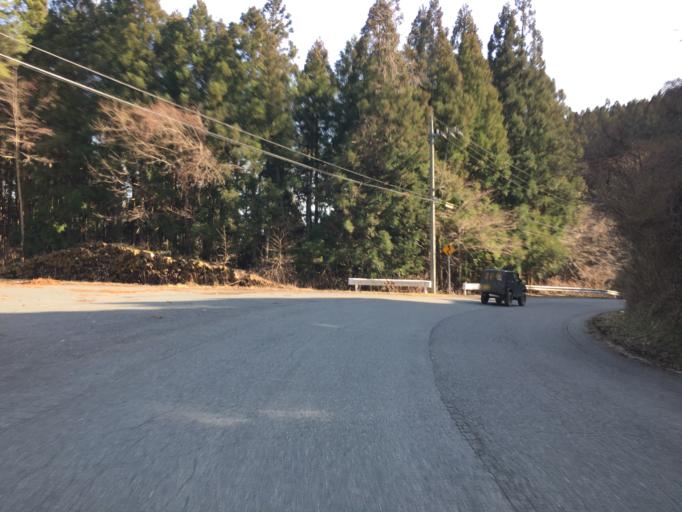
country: JP
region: Ibaraki
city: Takahagi
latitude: 36.8163
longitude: 140.5780
